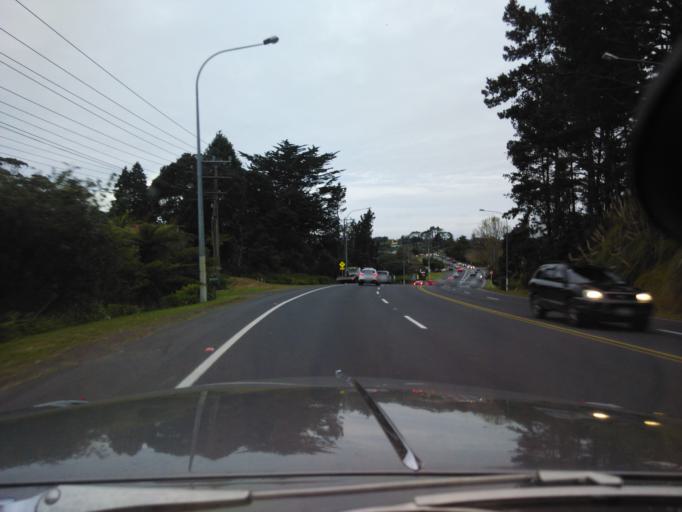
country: NZ
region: Auckland
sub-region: Auckland
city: Rothesay Bay
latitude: -36.7605
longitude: 174.7084
